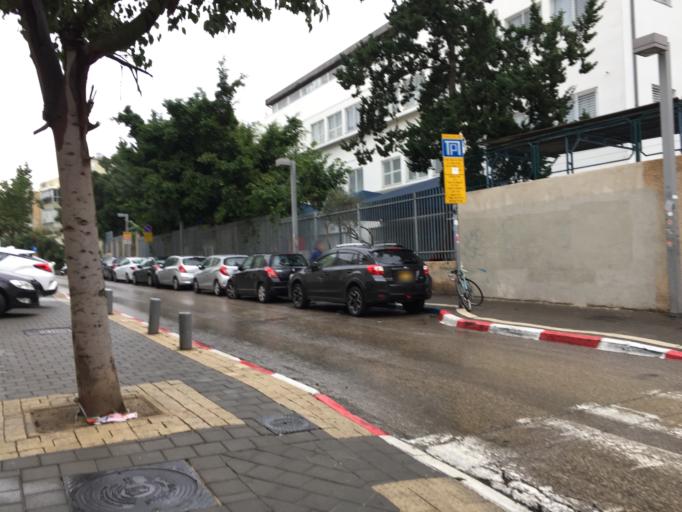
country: IL
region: Tel Aviv
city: Tel Aviv
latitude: 32.0673
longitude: 34.7726
